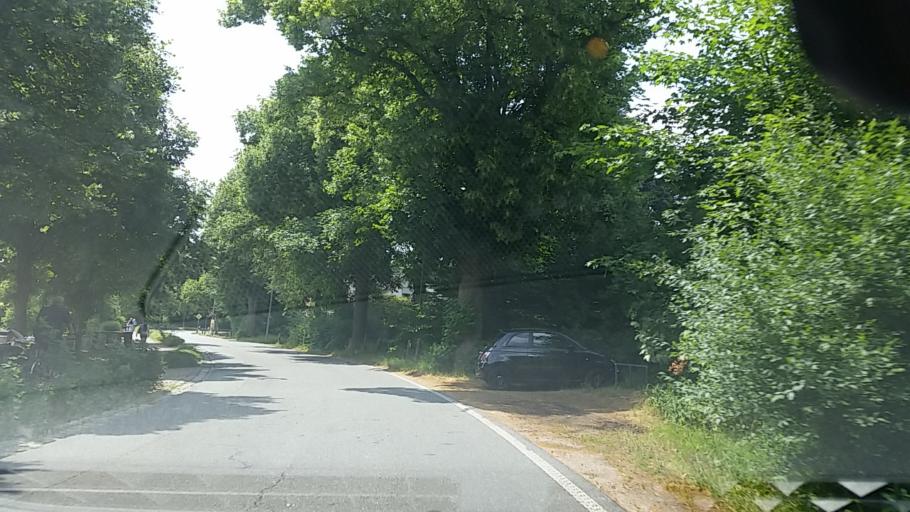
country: DE
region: Schleswig-Holstein
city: Bargteheide
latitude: 53.7343
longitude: 10.2824
